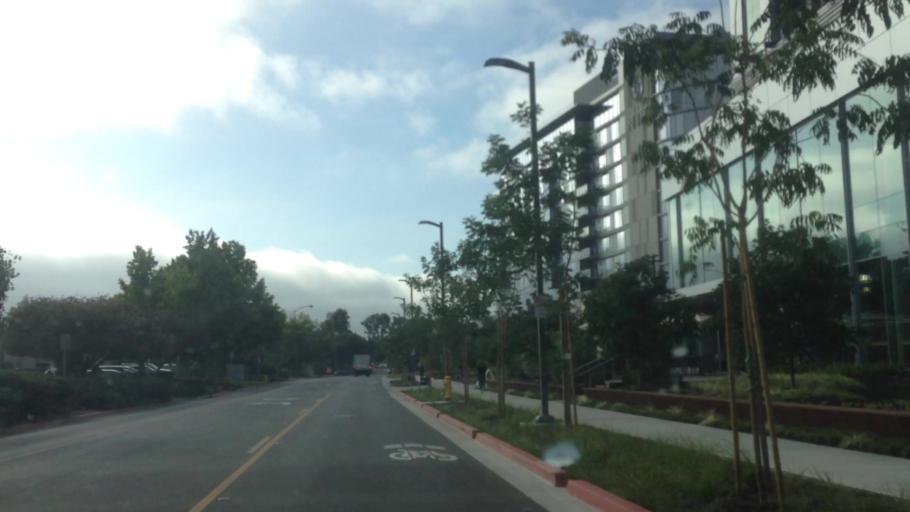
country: US
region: California
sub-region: San Mateo County
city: North Fair Oaks
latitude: 37.4834
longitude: -122.1778
